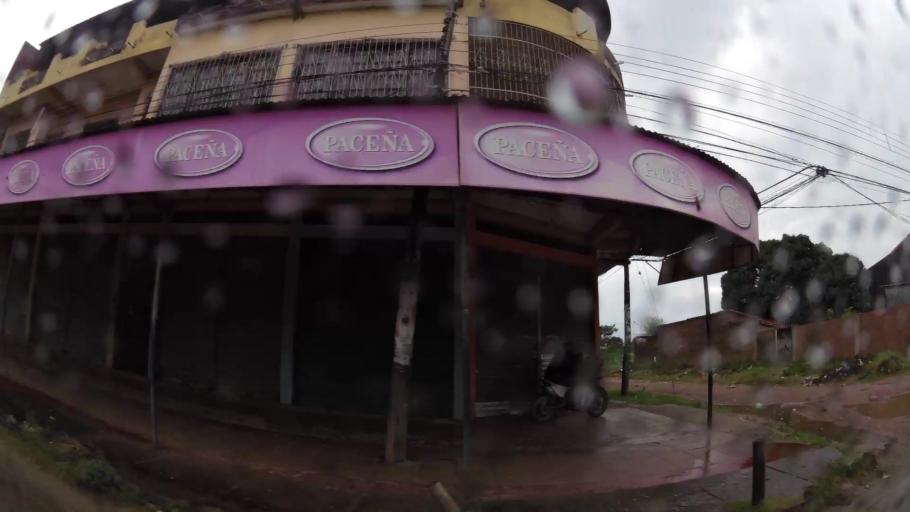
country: BO
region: Santa Cruz
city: Santa Cruz de la Sierra
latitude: -17.8077
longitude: -63.1286
